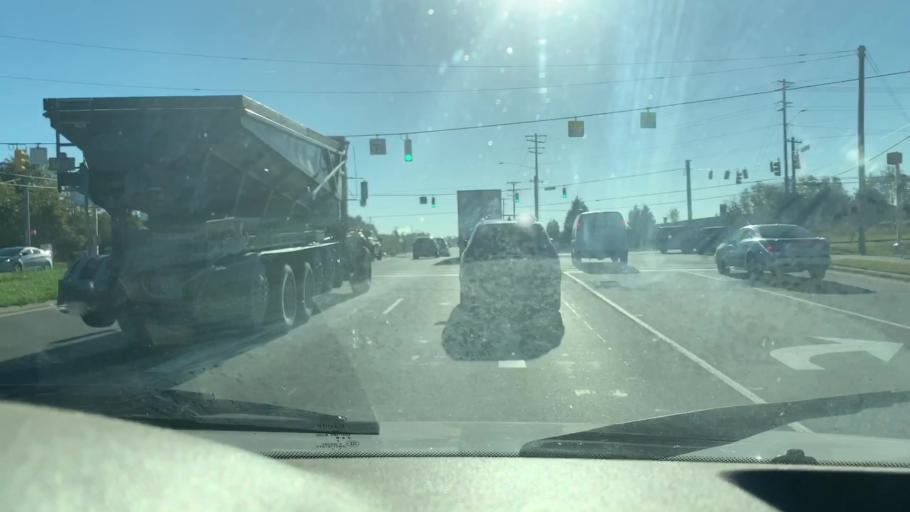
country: US
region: North Carolina
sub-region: Cabarrus County
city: Harrisburg
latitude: 35.4079
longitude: -80.7142
